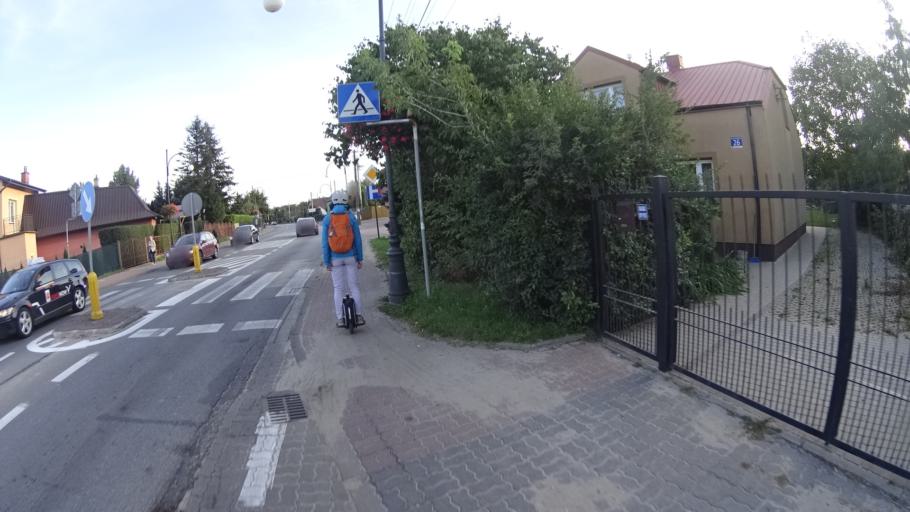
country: PL
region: Masovian Voivodeship
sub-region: Powiat legionowski
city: Nieporet
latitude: 52.4304
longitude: 21.0304
